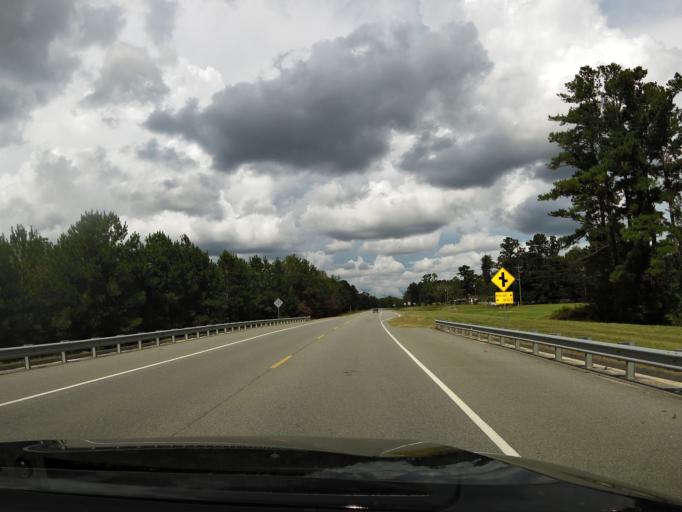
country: US
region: Georgia
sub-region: Brantley County
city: Nahunta
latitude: 31.1570
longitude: -81.9914
